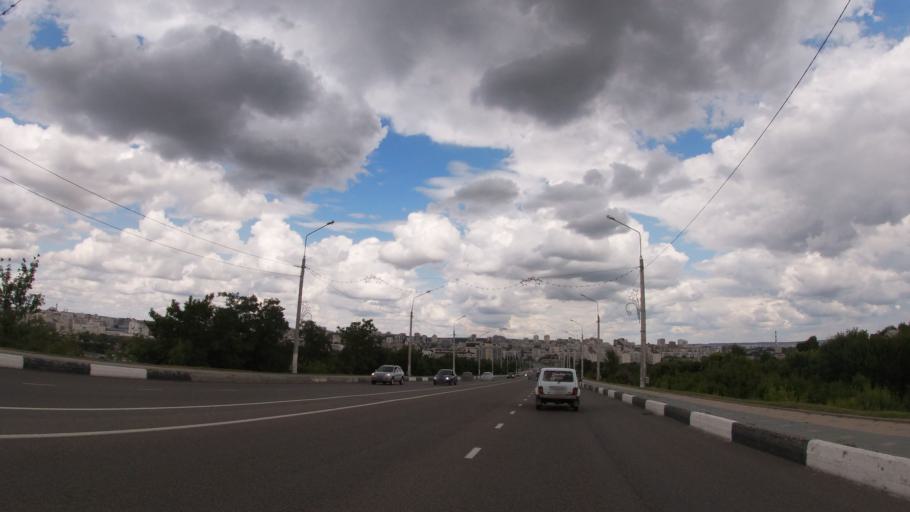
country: RU
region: Belgorod
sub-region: Belgorodskiy Rayon
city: Belgorod
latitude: 50.5828
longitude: 36.5846
